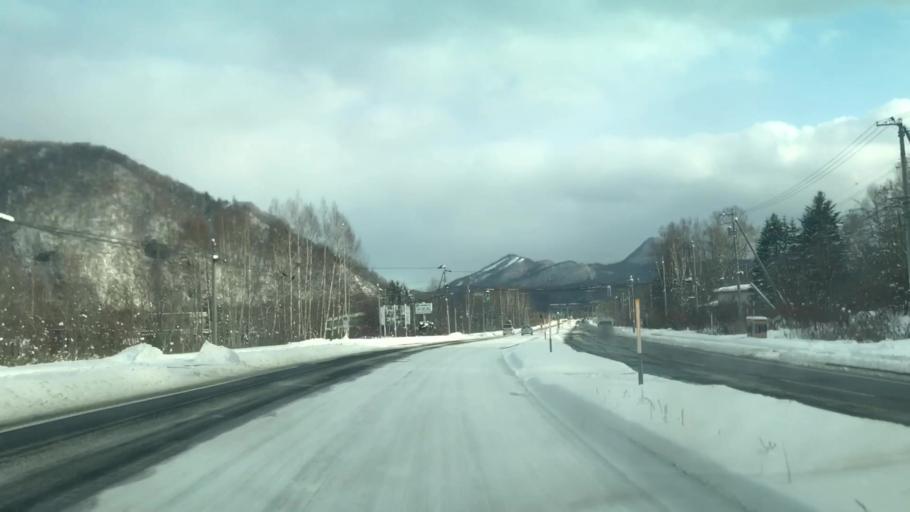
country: JP
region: Hokkaido
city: Sapporo
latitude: 42.9693
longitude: 141.2109
